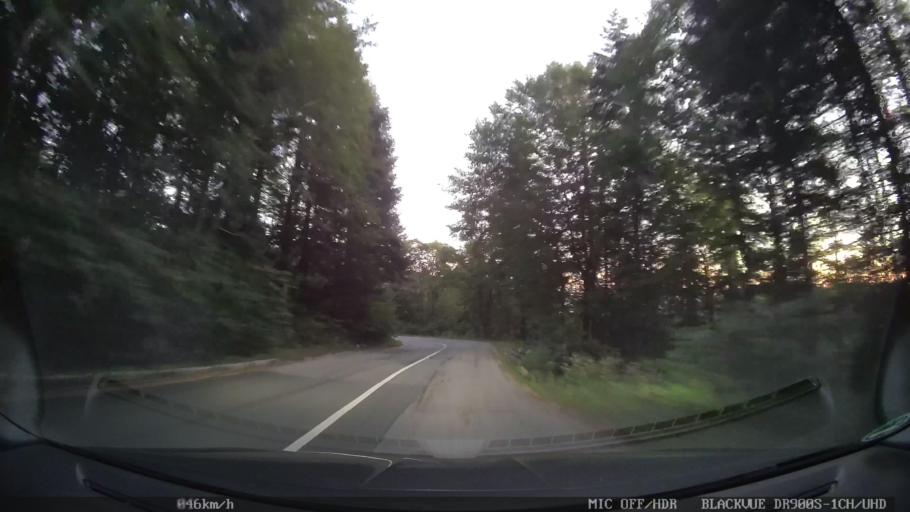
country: HR
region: Primorsko-Goranska
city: Novi Vinodolski
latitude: 45.1956
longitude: 14.8804
